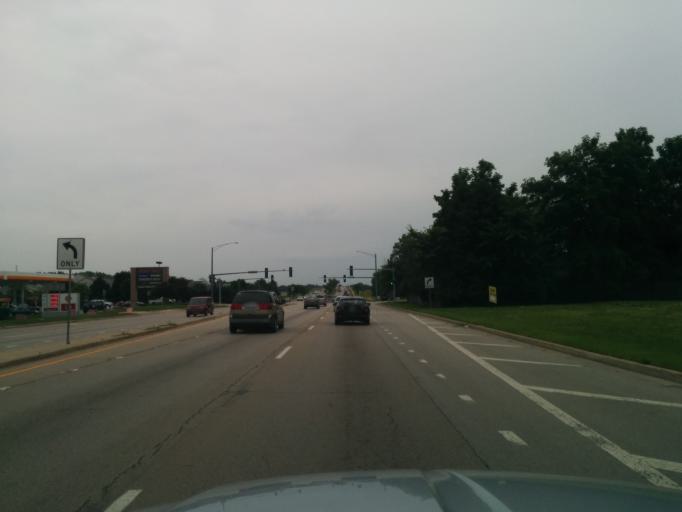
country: US
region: Illinois
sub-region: DuPage County
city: Warrenville
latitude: 41.7803
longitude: -88.2409
